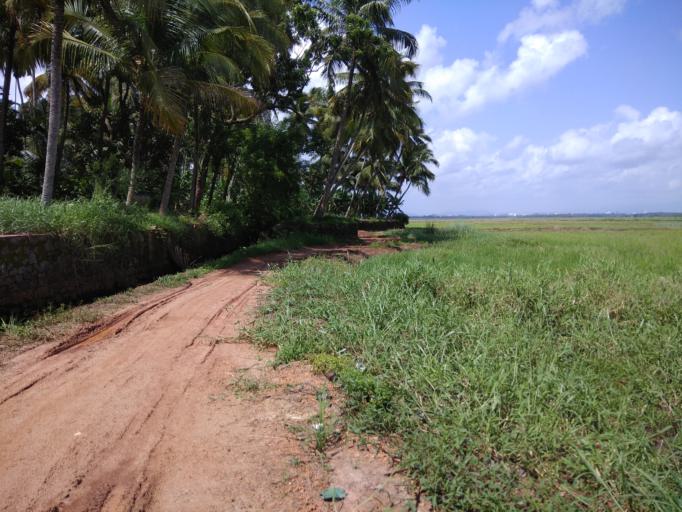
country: IN
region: Kerala
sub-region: Thrissur District
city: Trichur
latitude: 10.5355
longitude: 76.1439
